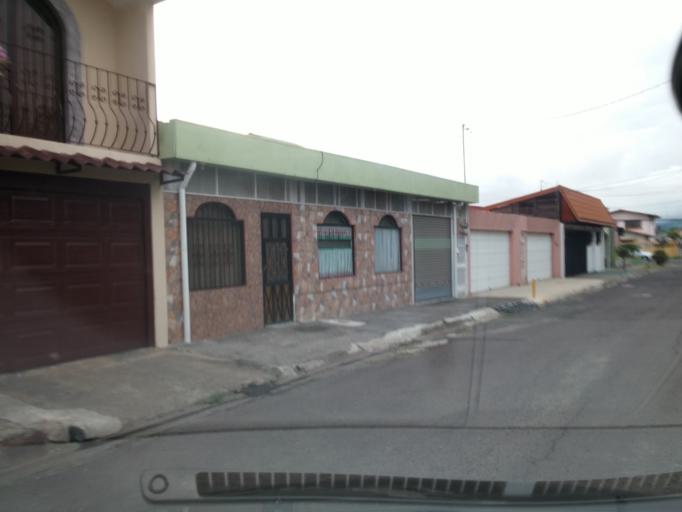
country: CR
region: Heredia
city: Heredia
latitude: 10.0133
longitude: -84.1191
